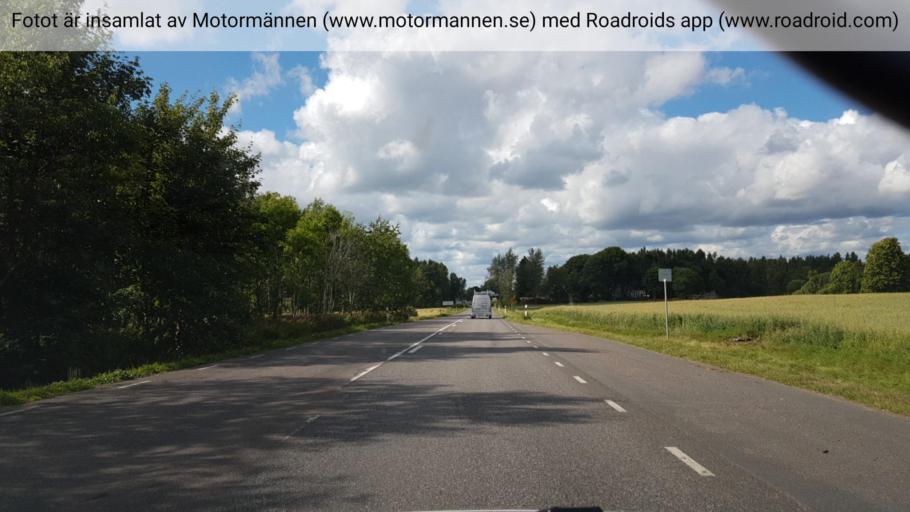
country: SE
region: Vaestra Goetaland
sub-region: Falkopings Kommun
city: Falkoeping
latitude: 58.0665
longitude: 13.5284
